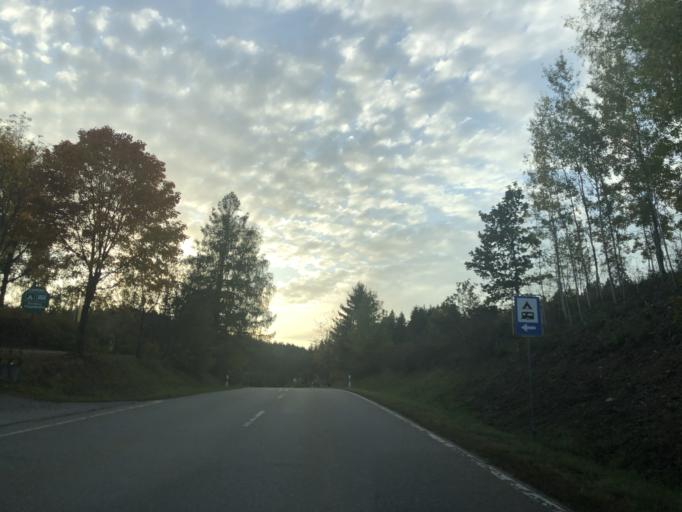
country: DE
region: Bavaria
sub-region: Lower Bavaria
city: Zwiesel
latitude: 49.0133
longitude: 13.2095
